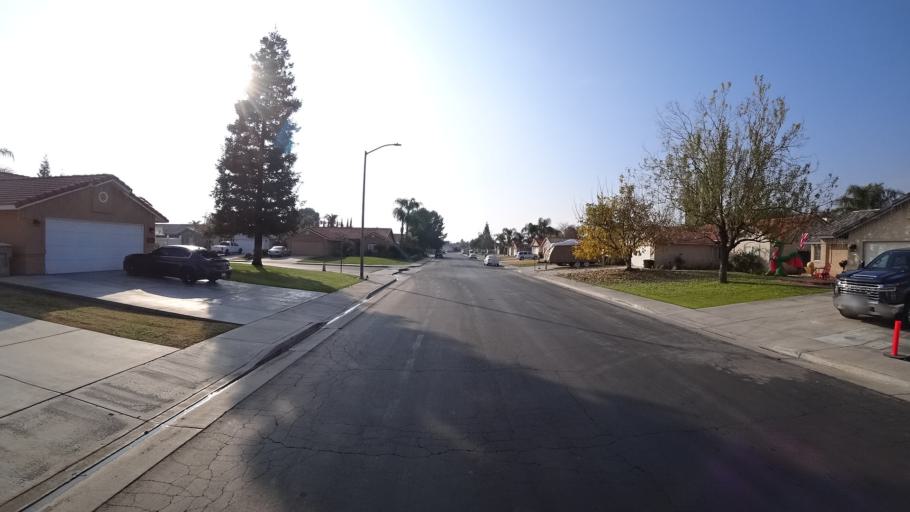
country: US
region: California
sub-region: Kern County
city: Greenfield
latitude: 35.3057
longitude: -119.0695
